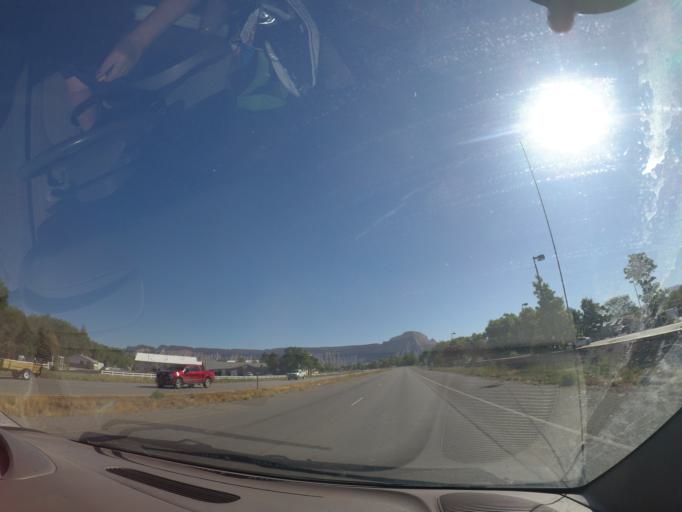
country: US
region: Colorado
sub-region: Mesa County
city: Clifton
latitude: 39.0927
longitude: -108.4522
